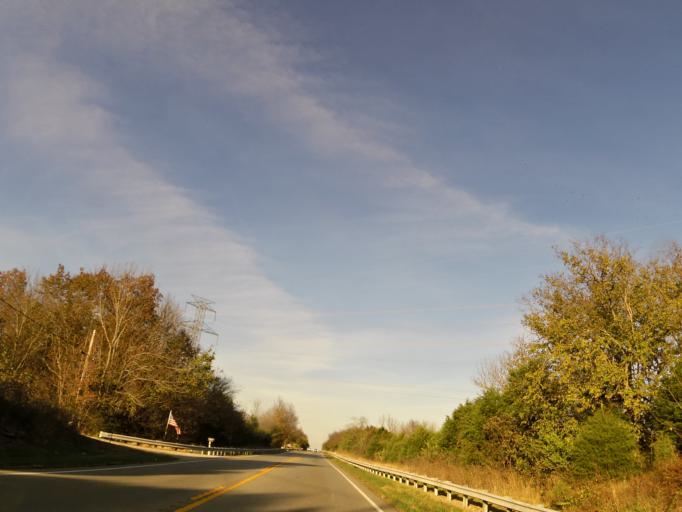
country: US
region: Kentucky
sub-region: Garrard County
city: Lancaster
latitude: 37.5740
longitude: -84.6133
